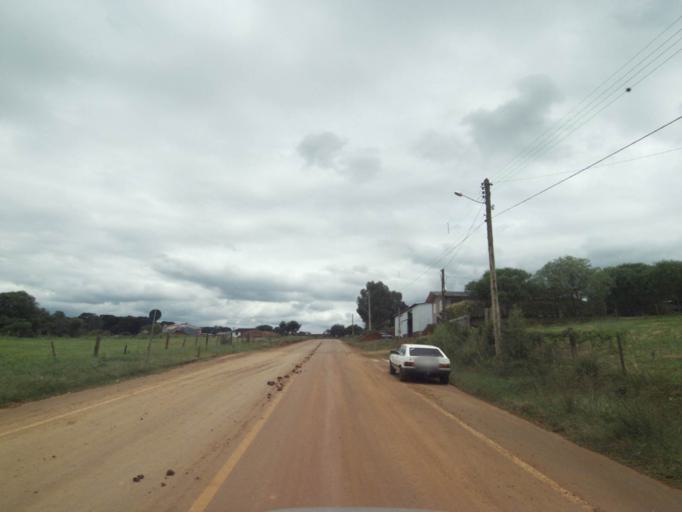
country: BR
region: Rio Grande do Sul
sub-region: Lagoa Vermelha
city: Lagoa Vermelha
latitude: -28.2131
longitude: -51.5451
